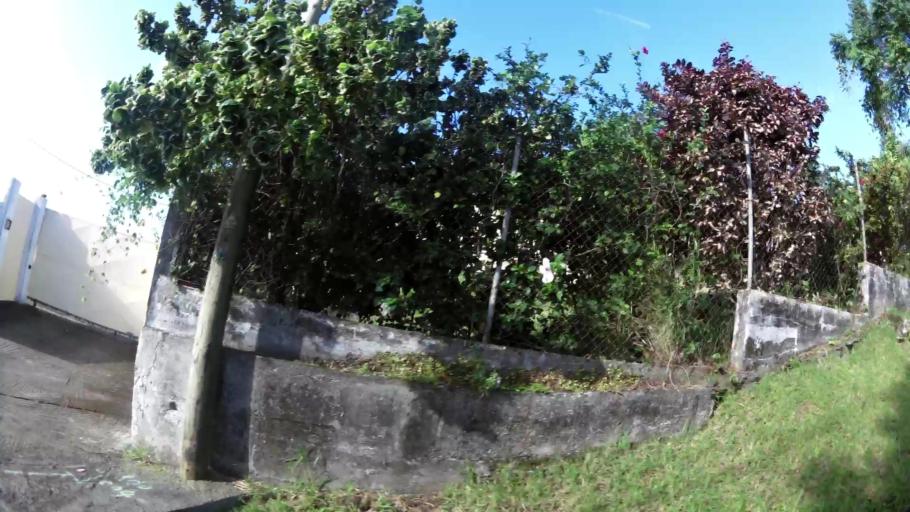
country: MQ
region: Martinique
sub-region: Martinique
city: Le Lamentin
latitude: 14.6294
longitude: -61.0285
